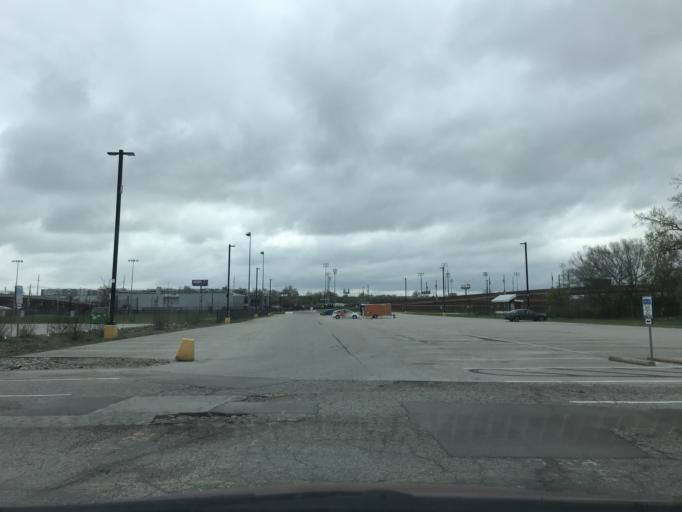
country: US
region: Kentucky
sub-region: Jefferson County
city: Audubon Park
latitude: 38.2122
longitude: -85.7600
